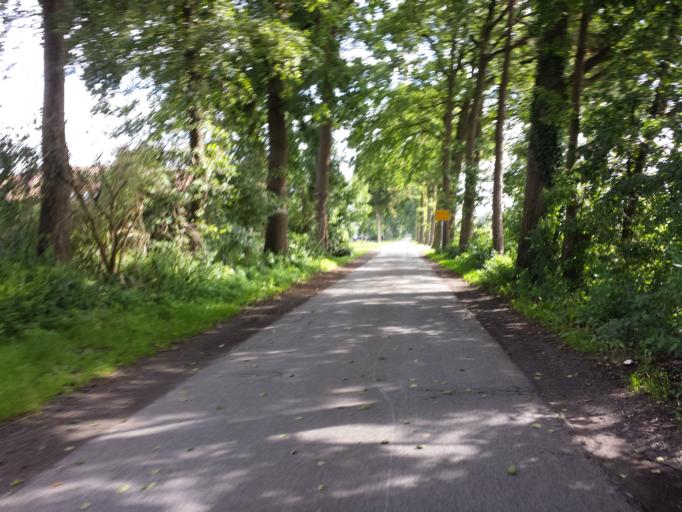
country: DE
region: North Rhine-Westphalia
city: Rietberg
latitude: 51.7912
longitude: 8.4921
